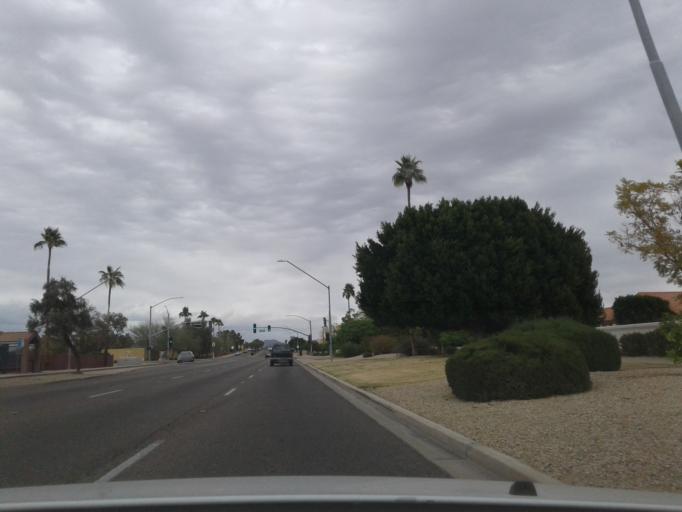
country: US
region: Arizona
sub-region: Maricopa County
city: Peoria
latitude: 33.6024
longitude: -112.1858
